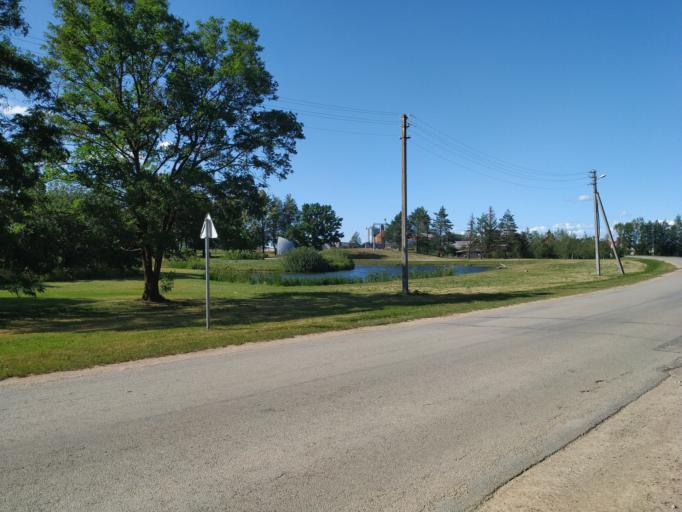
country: LT
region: Panevezys
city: Pasvalys
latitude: 56.1145
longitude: 24.3513
